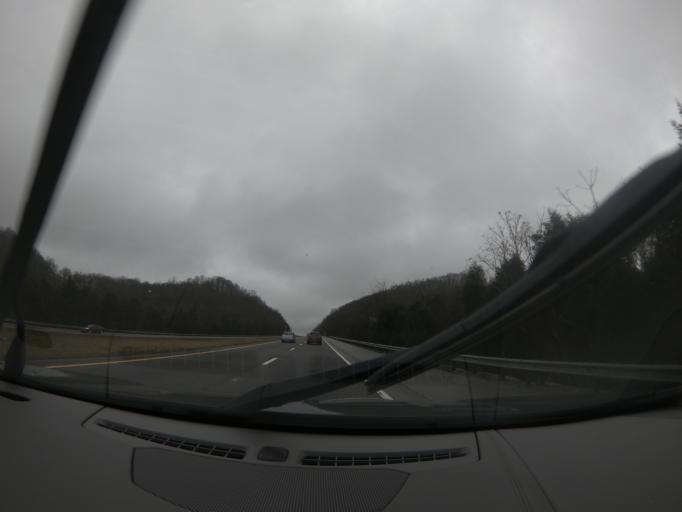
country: US
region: Tennessee
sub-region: Rutherford County
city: Plainview
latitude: 35.5967
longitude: -86.2396
